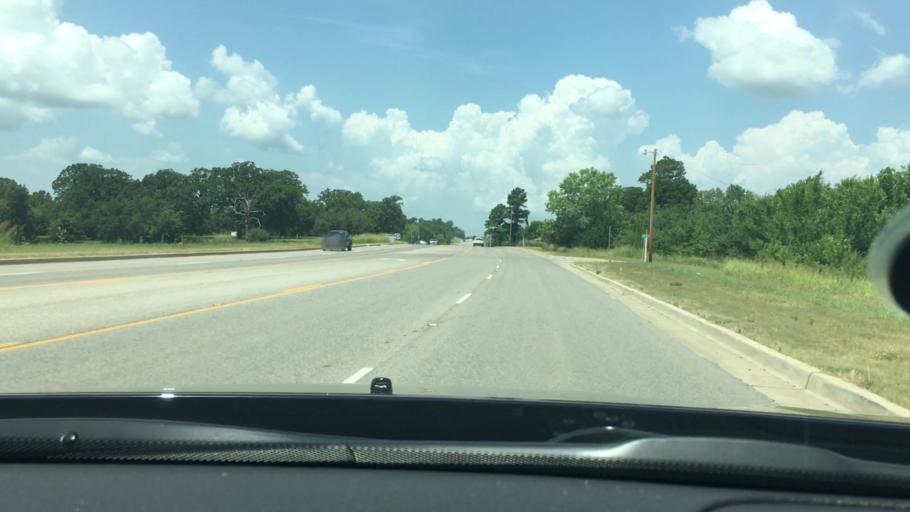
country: US
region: Oklahoma
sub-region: Marshall County
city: Oakland
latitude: 34.0999
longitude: -96.7867
